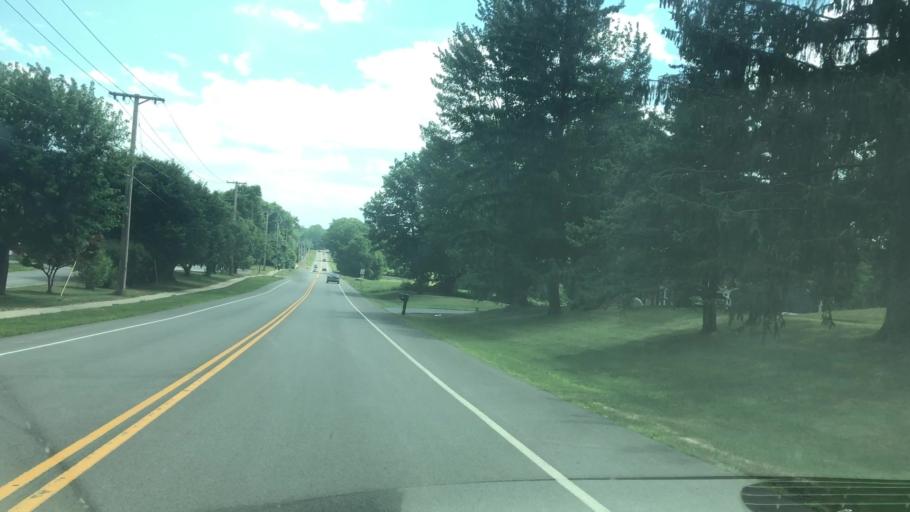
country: US
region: New York
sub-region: Monroe County
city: Fairport
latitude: 43.0794
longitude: -77.4020
